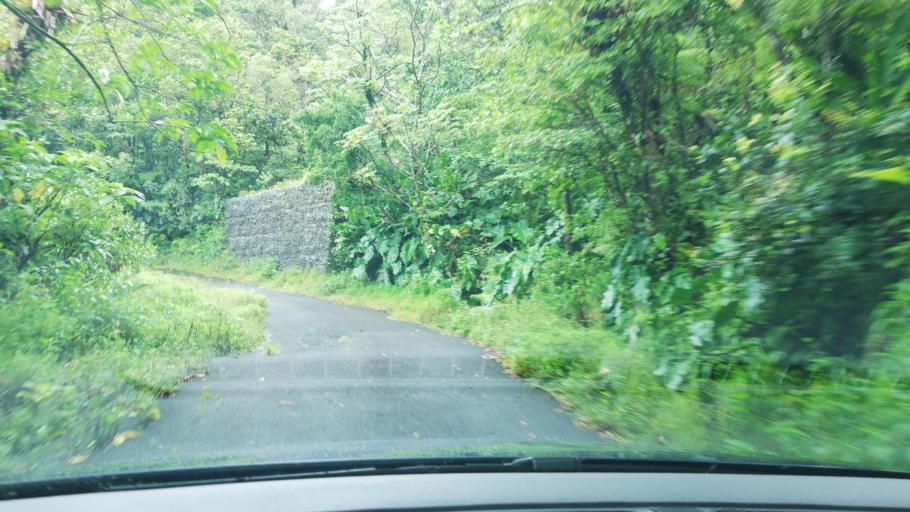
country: GP
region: Guadeloupe
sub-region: Guadeloupe
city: Saint-Claude
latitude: 16.0366
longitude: -61.6680
